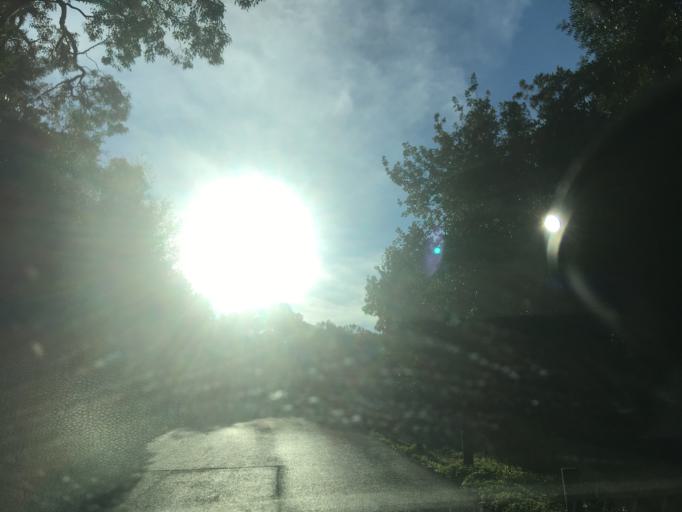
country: FR
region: Provence-Alpes-Cote d'Azur
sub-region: Departement du Var
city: Cavalaire-sur-Mer
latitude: 43.1564
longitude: 6.4813
